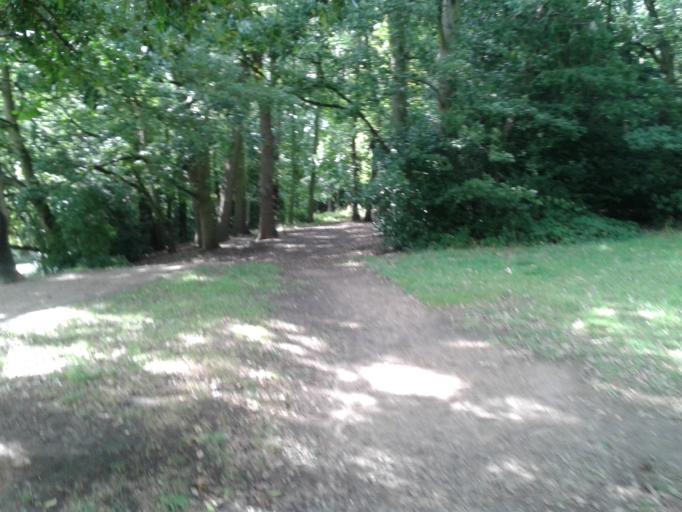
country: GB
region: England
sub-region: Greater London
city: Thornton Heath
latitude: 51.4230
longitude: -0.0646
